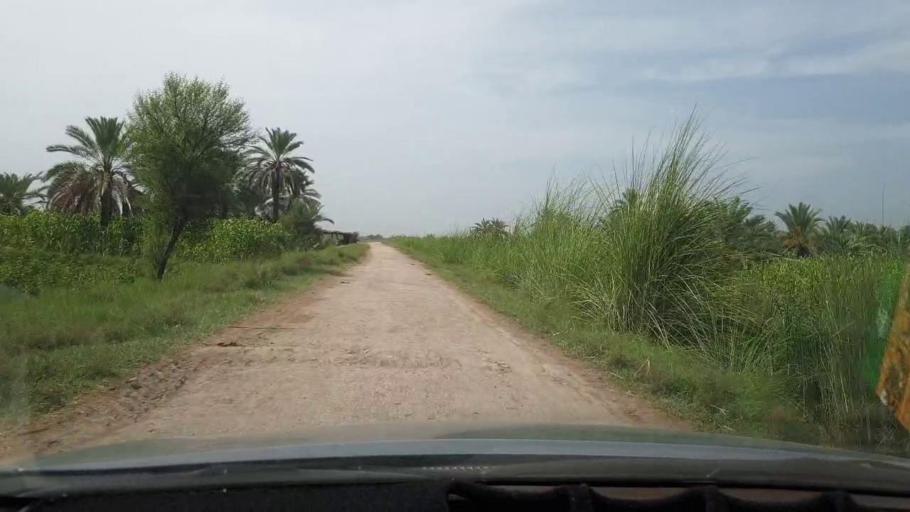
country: PK
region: Sindh
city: Khairpur
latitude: 27.4788
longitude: 68.7448
